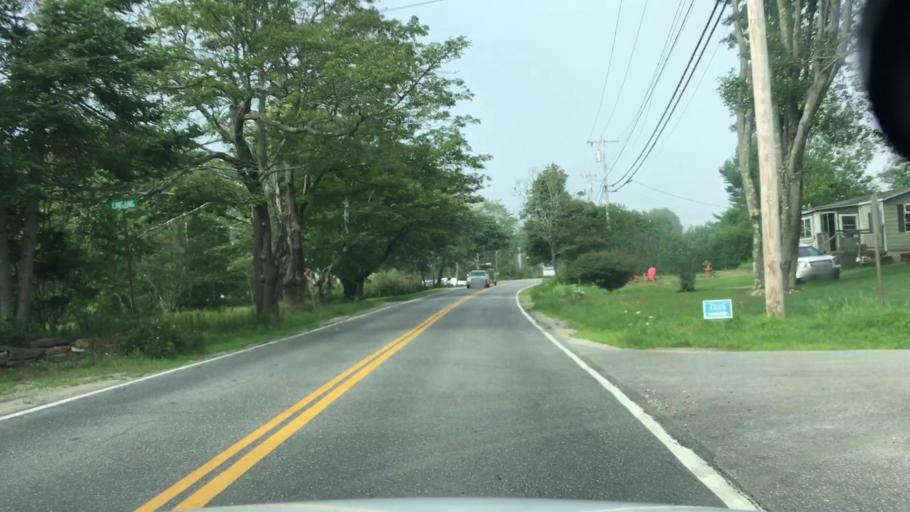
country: US
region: Maine
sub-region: Cumberland County
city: Harpswell Center
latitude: 43.7653
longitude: -69.9741
